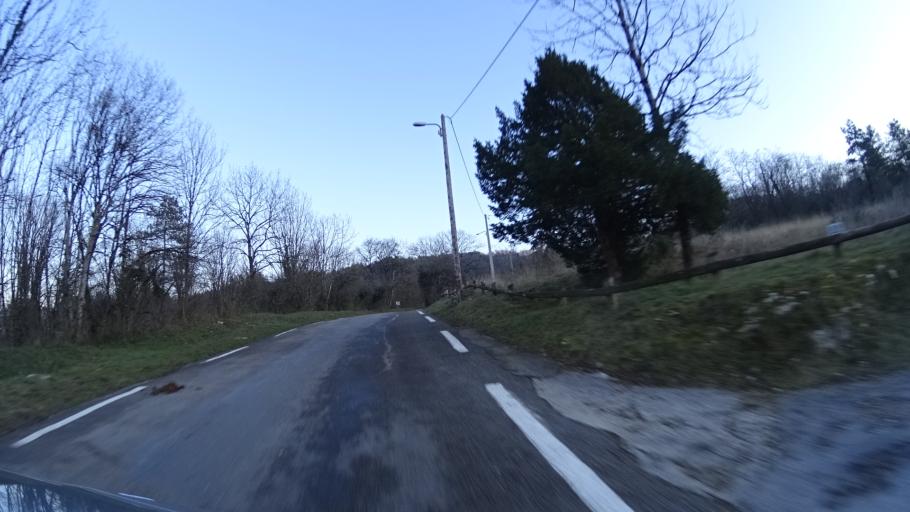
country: FR
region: Franche-Comte
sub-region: Departement du Doubs
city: Morre
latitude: 47.2228
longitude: 6.0424
